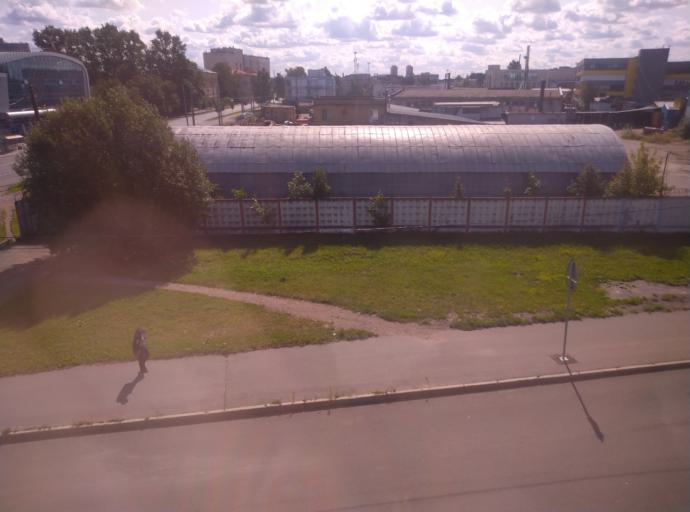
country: RU
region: St.-Petersburg
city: Centralniy
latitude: 59.9122
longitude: 30.3988
